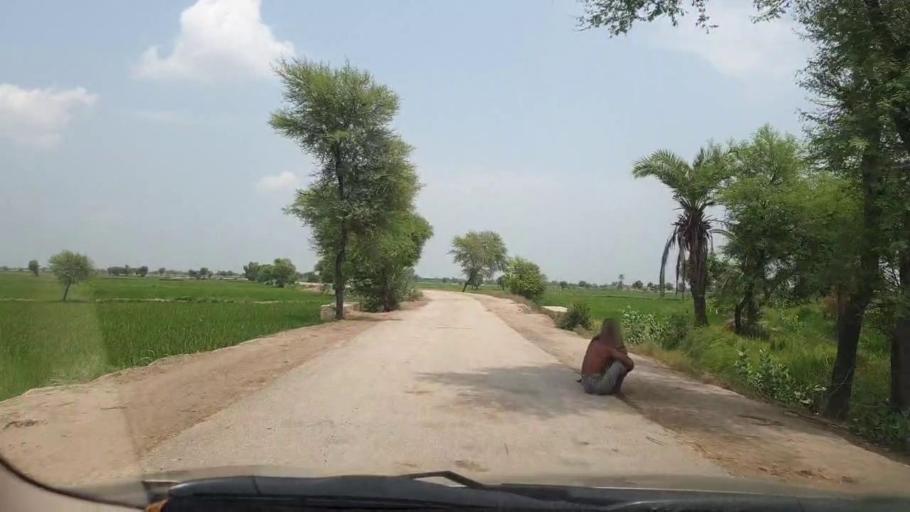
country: PK
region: Sindh
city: Larkana
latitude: 27.6011
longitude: 68.1420
